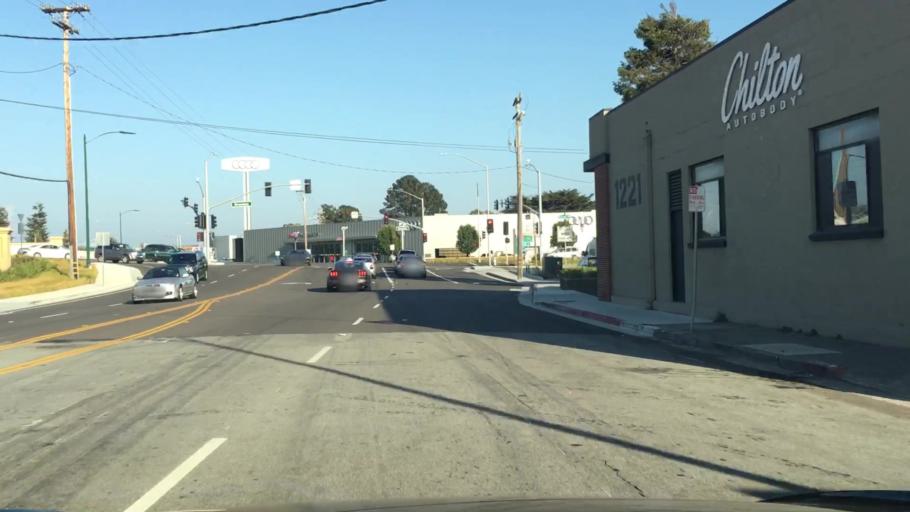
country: US
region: California
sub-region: San Mateo County
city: Burlingame
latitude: 37.5894
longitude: -122.3634
